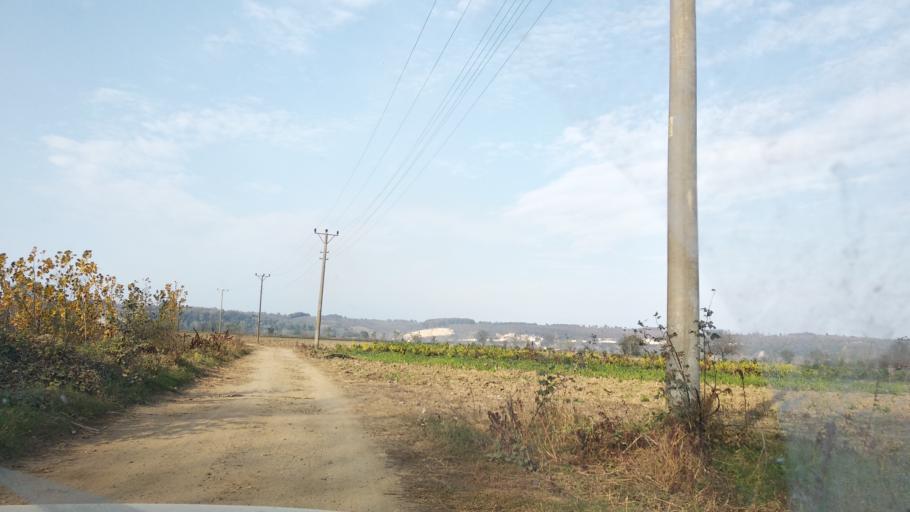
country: TR
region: Sakarya
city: Karasu
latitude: 41.0846
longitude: 30.6023
